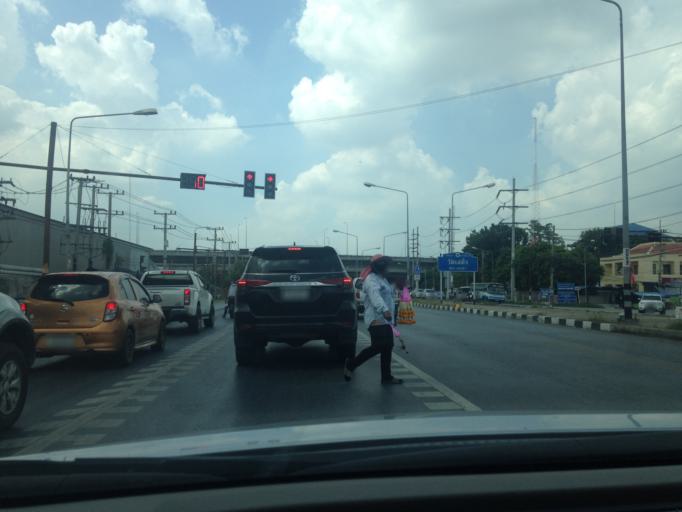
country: TH
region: Phra Nakhon Si Ayutthaya
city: Ban Bang Kadi Pathum Thani
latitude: 14.0002
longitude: 100.5704
